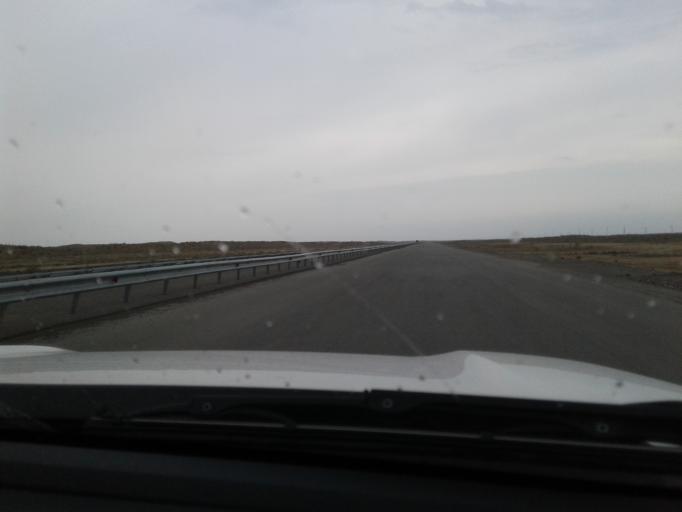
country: TM
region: Ahal
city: Abadan
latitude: 38.5658
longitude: 58.5069
